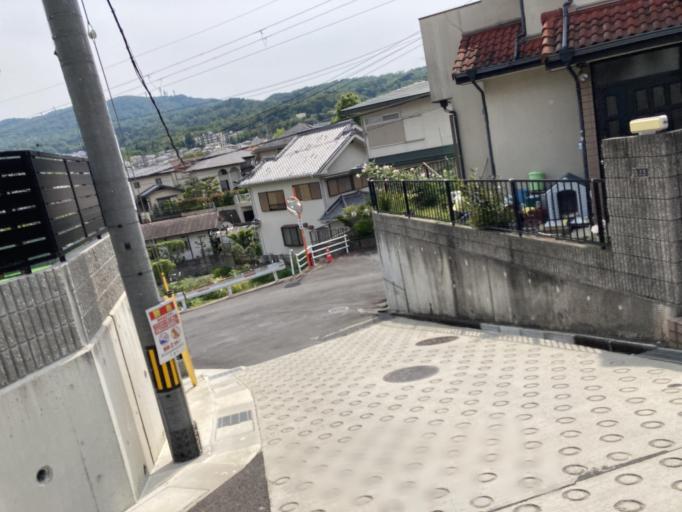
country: JP
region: Nara
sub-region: Ikoma-shi
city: Ikoma
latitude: 34.7095
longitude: 135.6957
